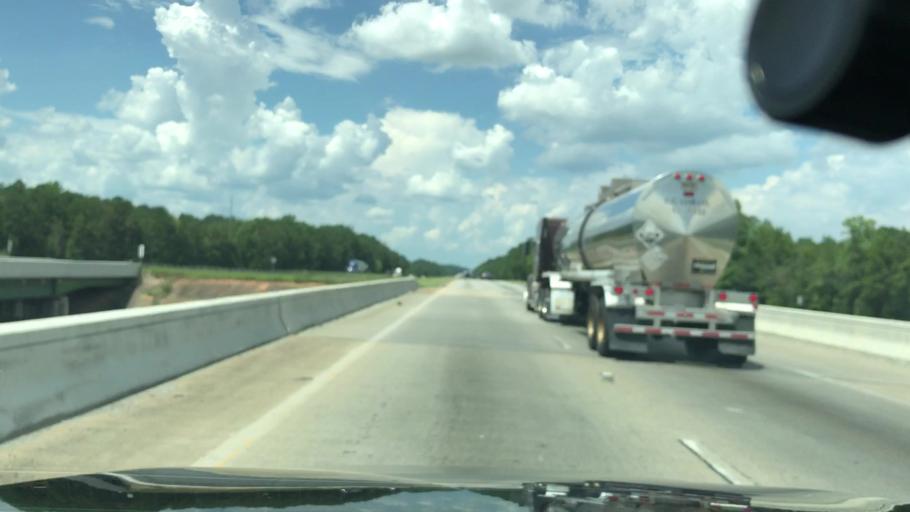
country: US
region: South Carolina
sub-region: Chester County
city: Eureka Mill
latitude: 34.7123
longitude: -81.0310
